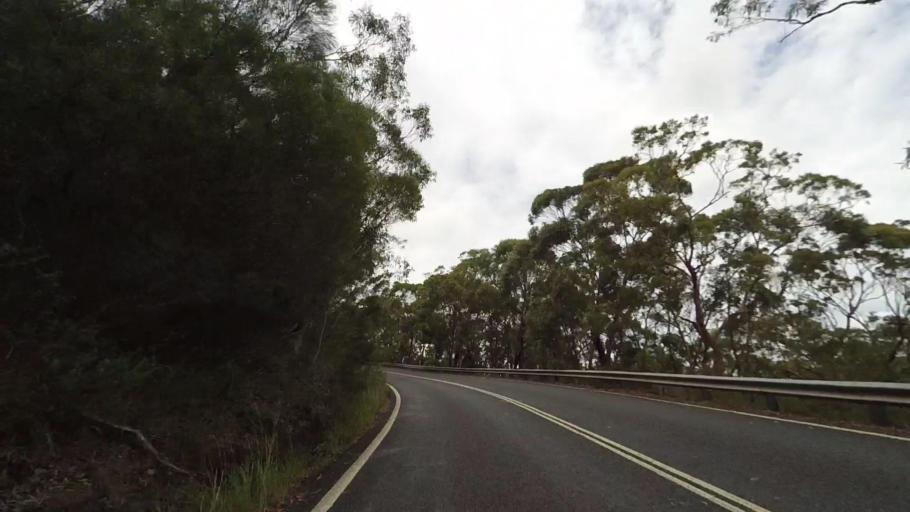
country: AU
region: New South Wales
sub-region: Sutherland Shire
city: Grays Point
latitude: -34.0804
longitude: 151.0568
